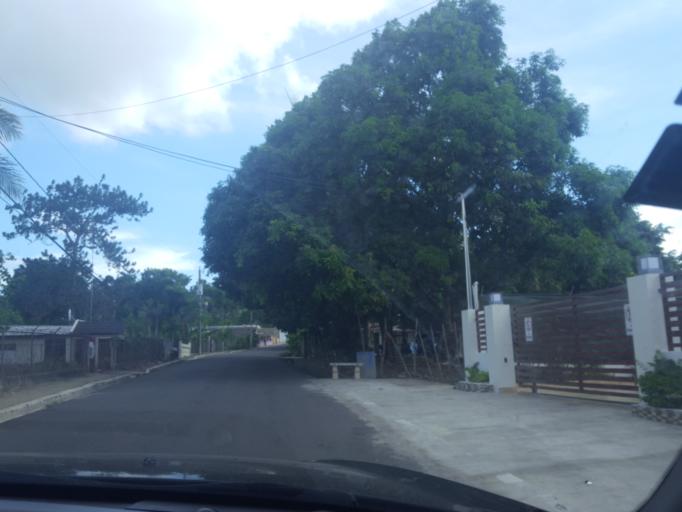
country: DO
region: Santiago
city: Licey al Medio
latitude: 19.3717
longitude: -70.6301
